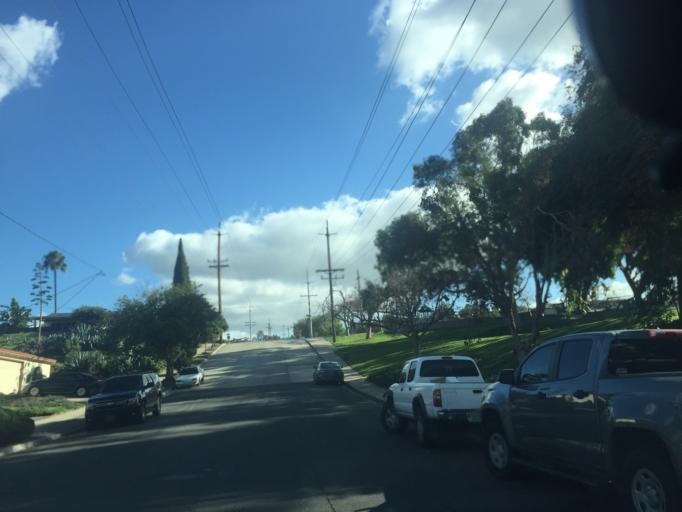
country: US
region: California
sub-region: San Diego County
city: La Mesa
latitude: 32.7877
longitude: -117.0950
